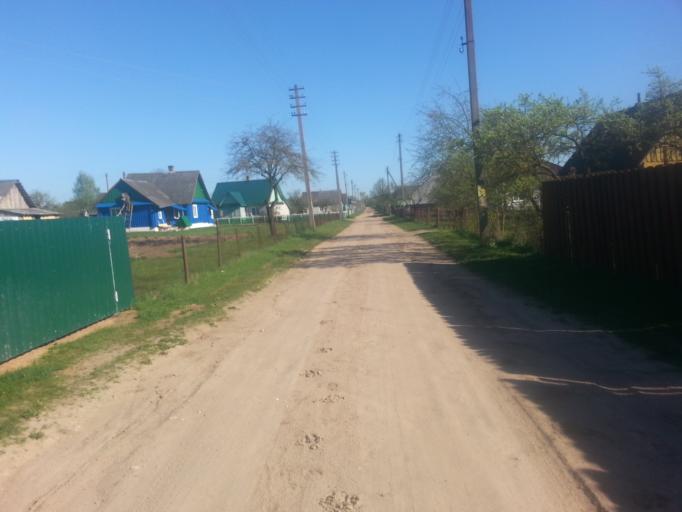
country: BY
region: Minsk
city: Narach
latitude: 54.9342
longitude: 26.6789
